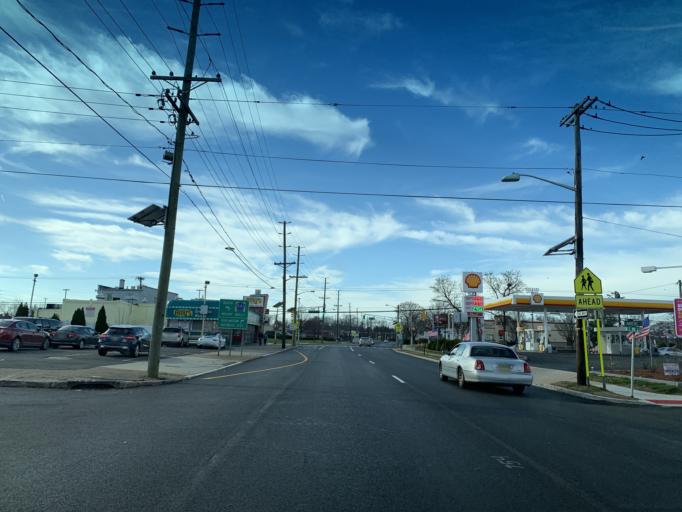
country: US
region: New Jersey
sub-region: Burlington County
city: Burlington
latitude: 40.0720
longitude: -74.8544
